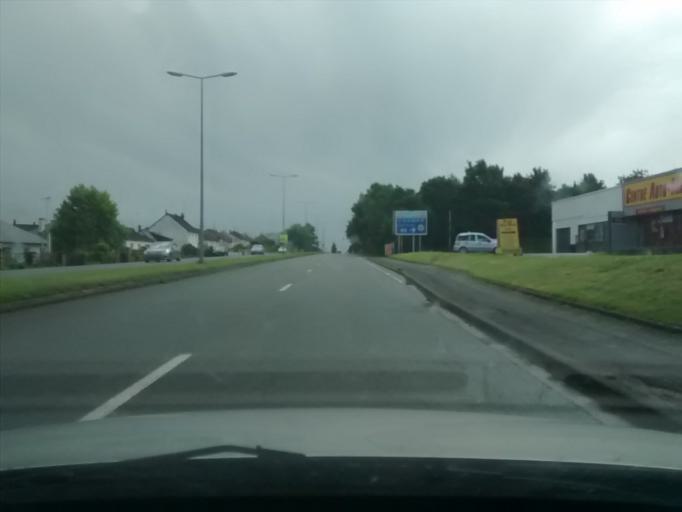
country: FR
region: Pays de la Loire
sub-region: Departement de la Mayenne
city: Laval
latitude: 48.0605
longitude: -0.7803
